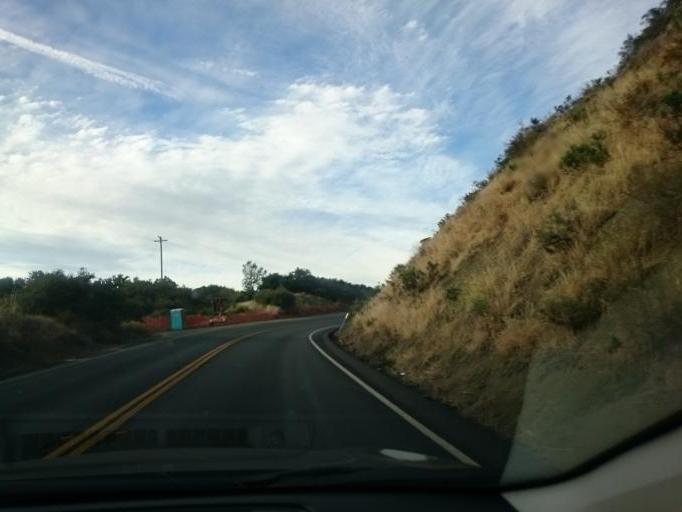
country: US
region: California
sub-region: Yolo County
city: Winters
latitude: 38.4690
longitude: -122.1466
